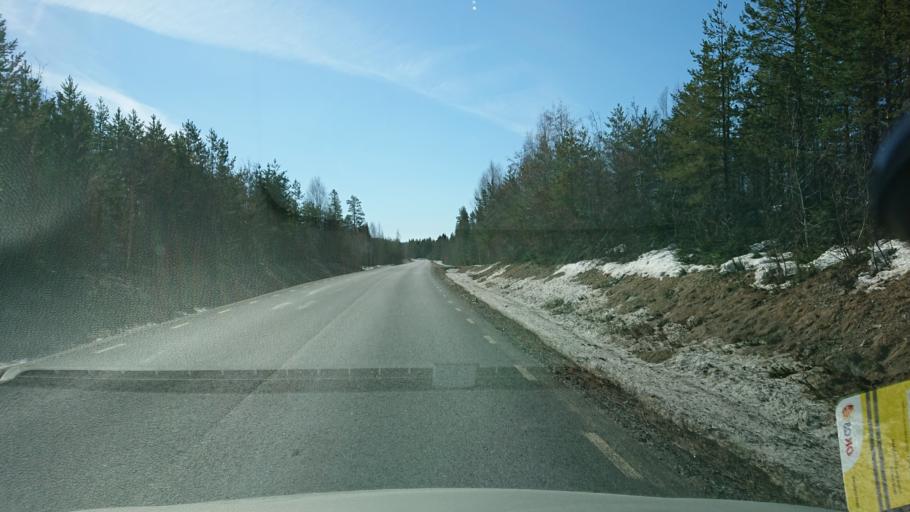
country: SE
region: Vaesterbotten
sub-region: Dorotea Kommun
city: Dorotea
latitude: 64.0895
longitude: 16.2602
